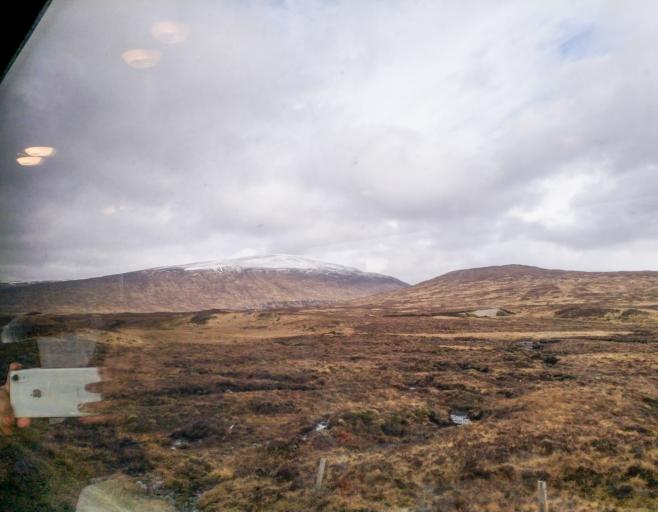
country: GB
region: Scotland
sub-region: Highland
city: Spean Bridge
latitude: 56.7437
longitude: -4.6689
